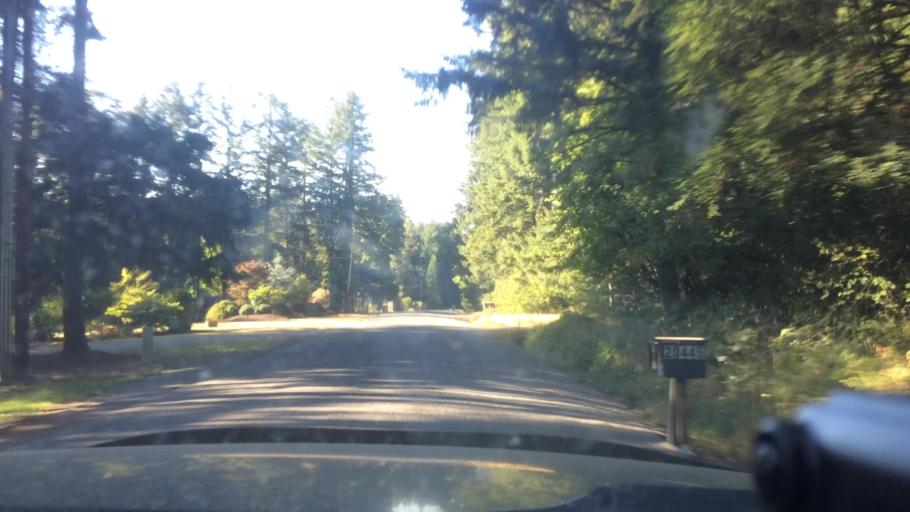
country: US
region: Oregon
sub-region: Yamhill County
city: Newberg
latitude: 45.3743
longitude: -122.9754
